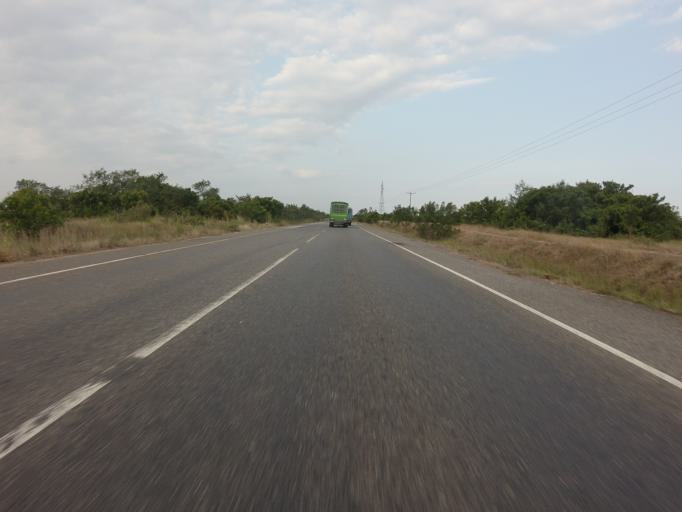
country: GH
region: Volta
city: Anloga
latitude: 6.0899
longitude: 0.5242
